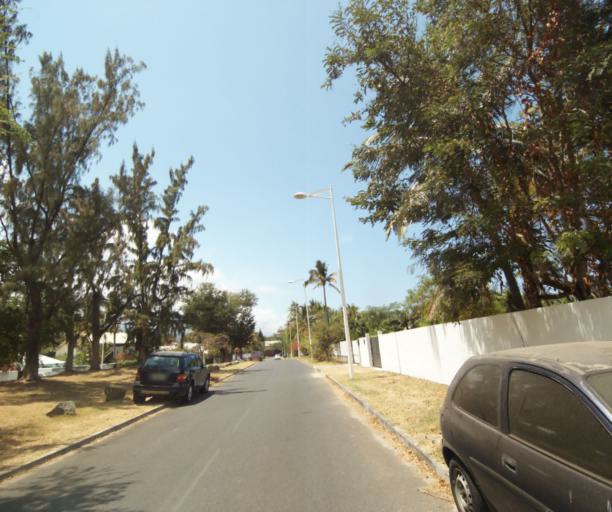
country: RE
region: Reunion
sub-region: Reunion
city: Trois-Bassins
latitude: -21.0777
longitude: 55.2274
